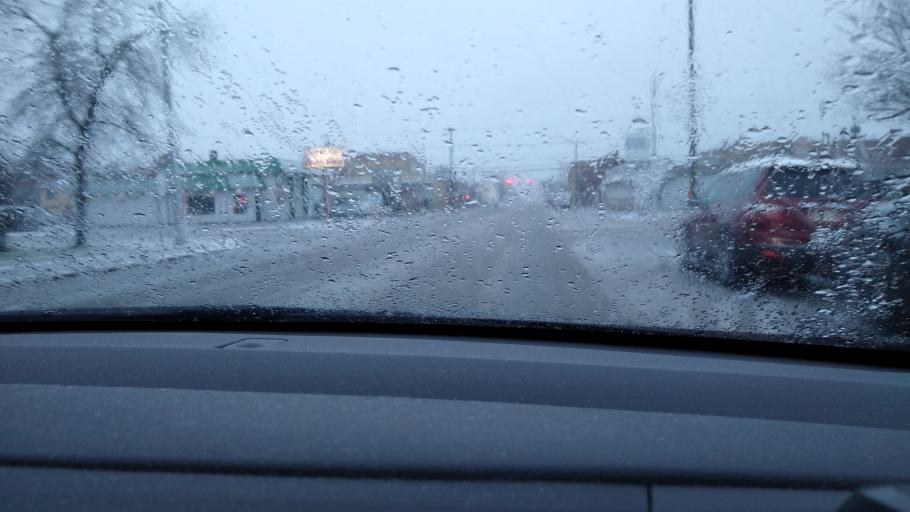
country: US
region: Michigan
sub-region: Delta County
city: Escanaba
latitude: 45.7443
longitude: -87.0612
